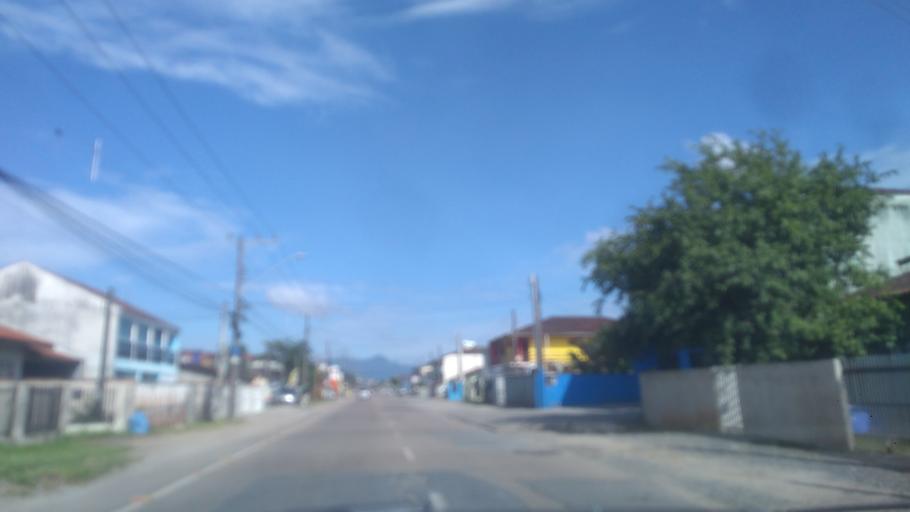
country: BR
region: Santa Catarina
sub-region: Joinville
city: Joinville
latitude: -26.3213
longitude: -48.8127
